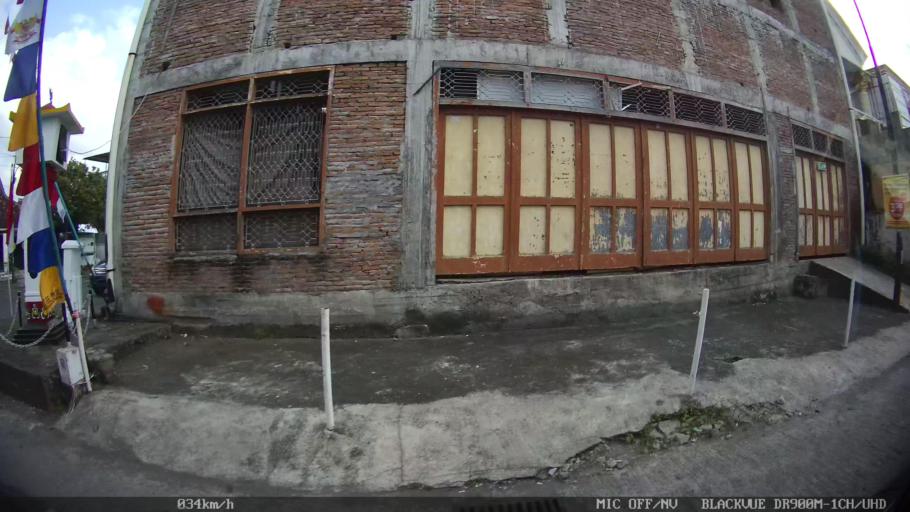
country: ID
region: Daerah Istimewa Yogyakarta
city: Kasihan
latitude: -7.8211
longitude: 110.3632
